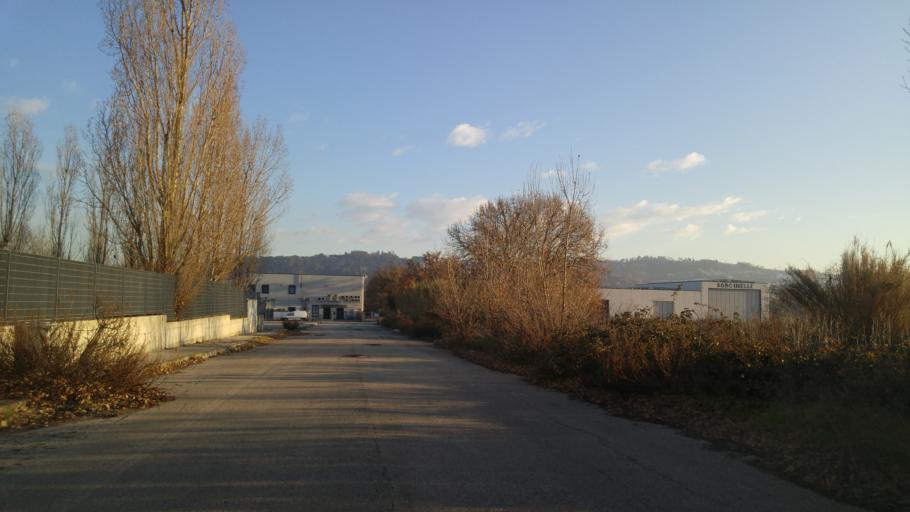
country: IT
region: The Marches
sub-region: Provincia di Ancona
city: Monterado
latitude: 43.7091
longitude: 13.0755
